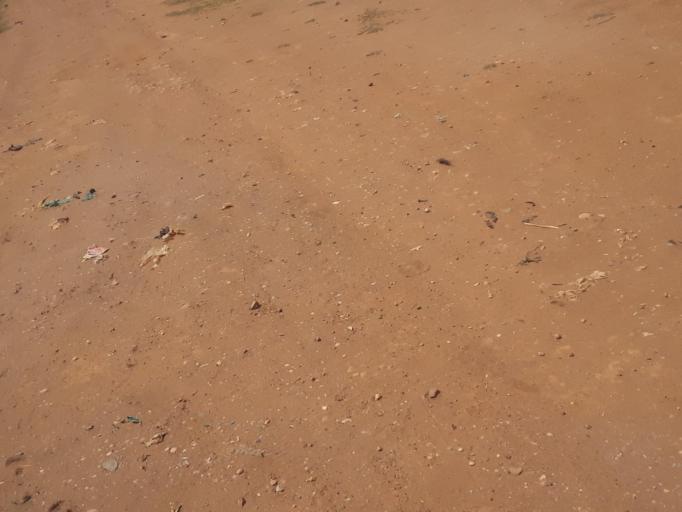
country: ZM
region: Lusaka
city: Lusaka
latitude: -15.3556
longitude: 28.2815
